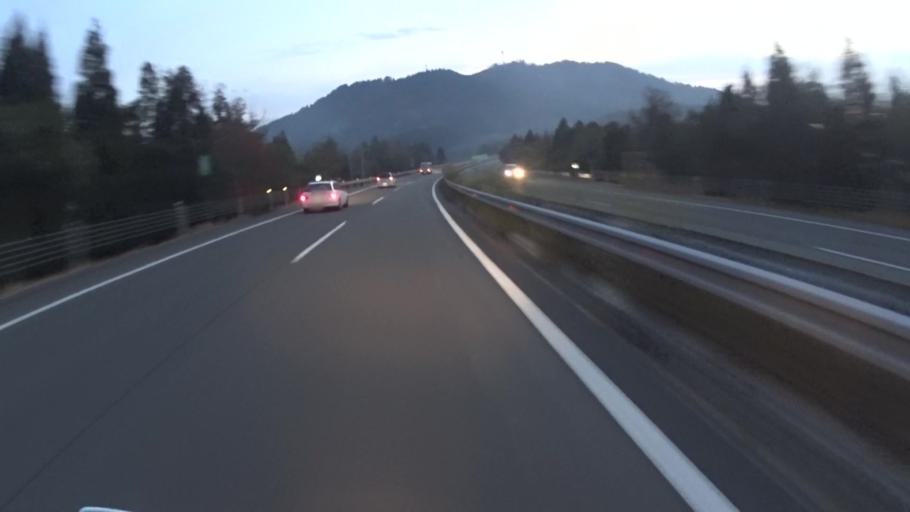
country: JP
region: Kyoto
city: Ayabe
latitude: 35.3590
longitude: 135.3069
